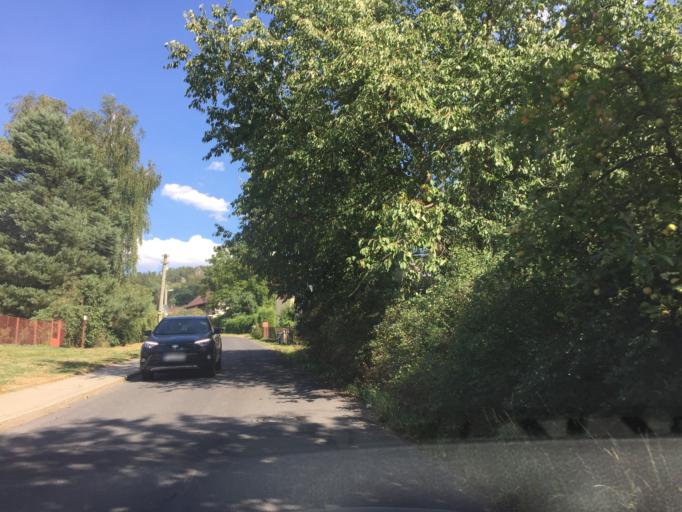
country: CZ
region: Liberecky
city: Mala Skala
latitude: 50.6376
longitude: 15.1941
